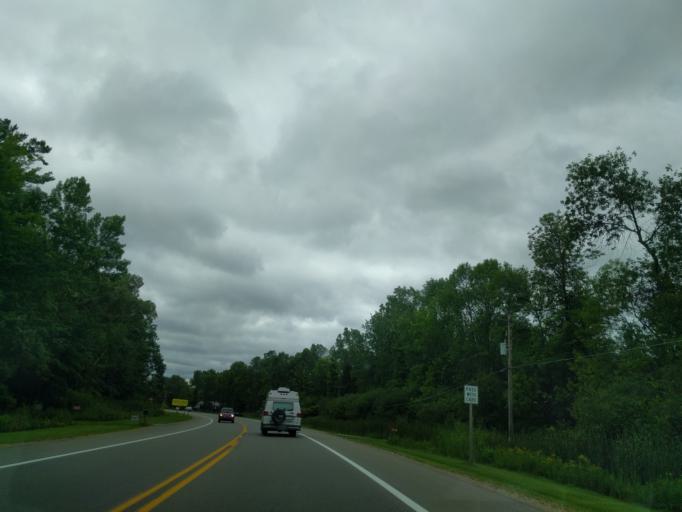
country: US
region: Michigan
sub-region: Menominee County
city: Menominee
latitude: 45.1500
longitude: -87.6021
